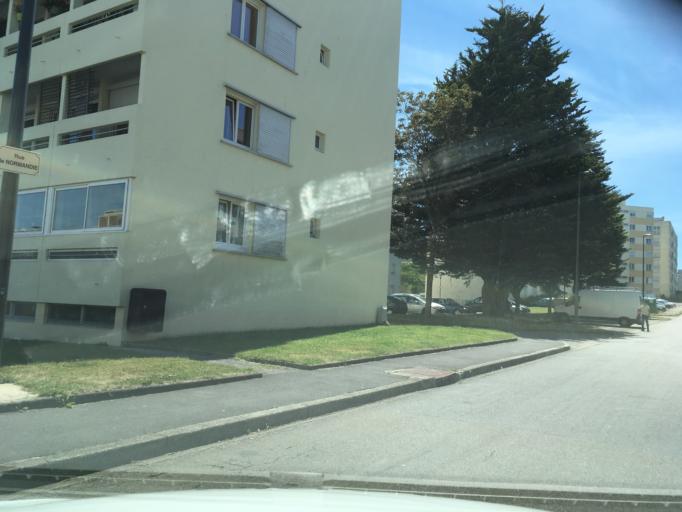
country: FR
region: Brittany
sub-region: Departement du Finistere
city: Quimper
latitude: 47.9867
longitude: -4.1246
